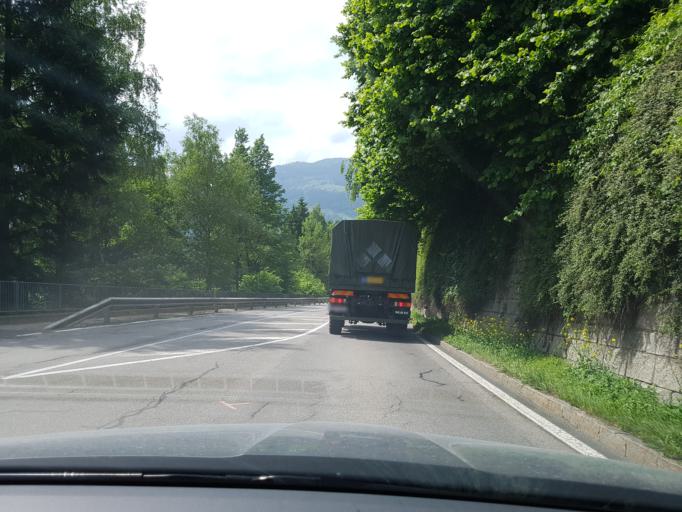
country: AT
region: Carinthia
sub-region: Politischer Bezirk Spittal an der Drau
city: Radenthein
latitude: 46.7973
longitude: 13.7250
